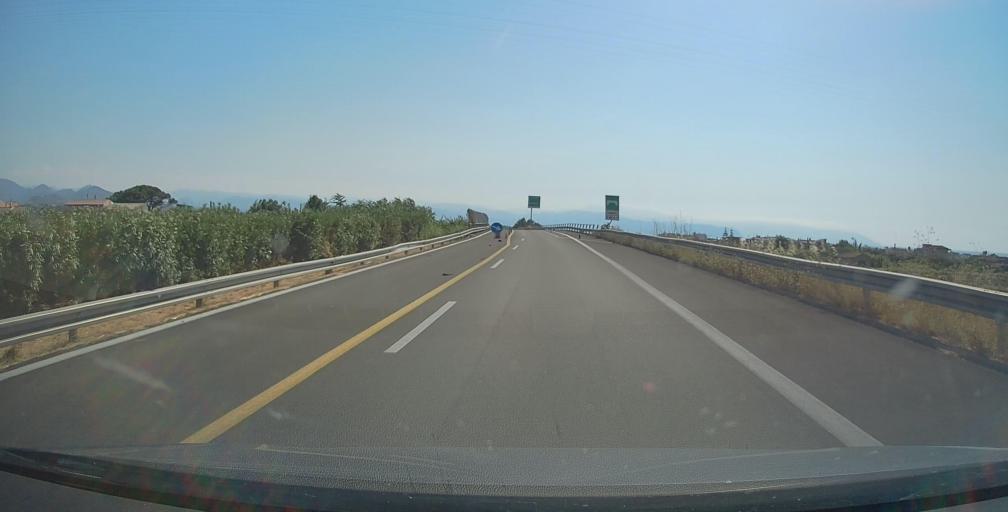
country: IT
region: Sicily
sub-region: Messina
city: Barcellona Pozzo di Gotto
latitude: 38.1633
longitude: 15.2015
